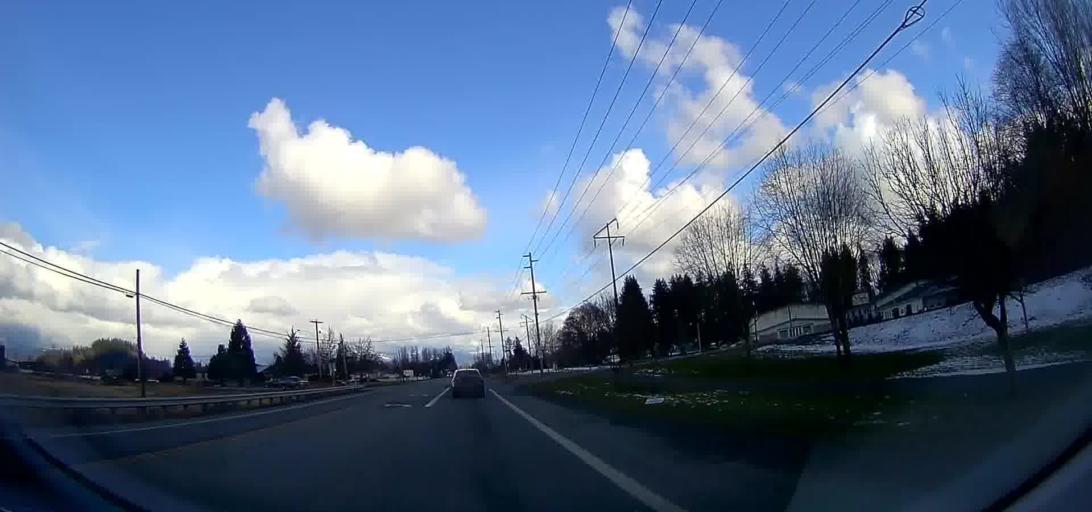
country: US
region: Washington
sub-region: Skagit County
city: Burlington
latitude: 48.4803
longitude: -122.3146
